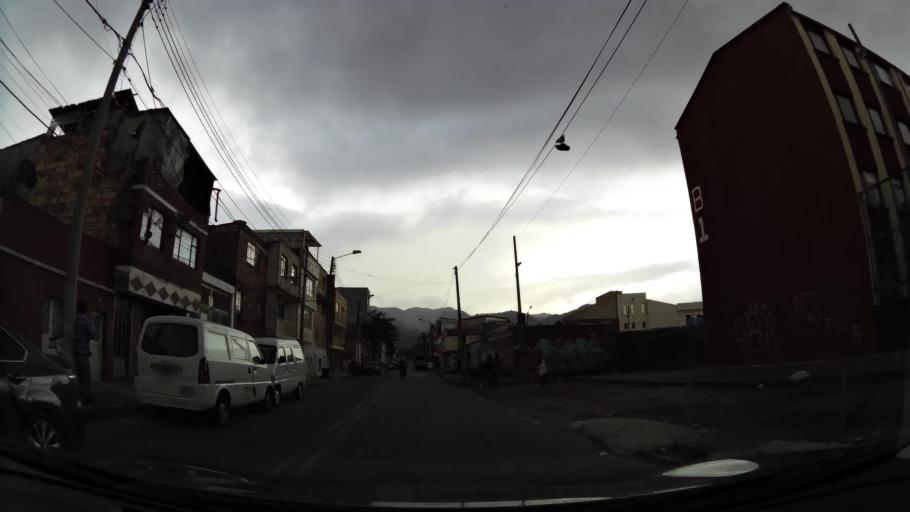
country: CO
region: Bogota D.C.
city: Barrio San Luis
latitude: 4.6728
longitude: -74.0753
